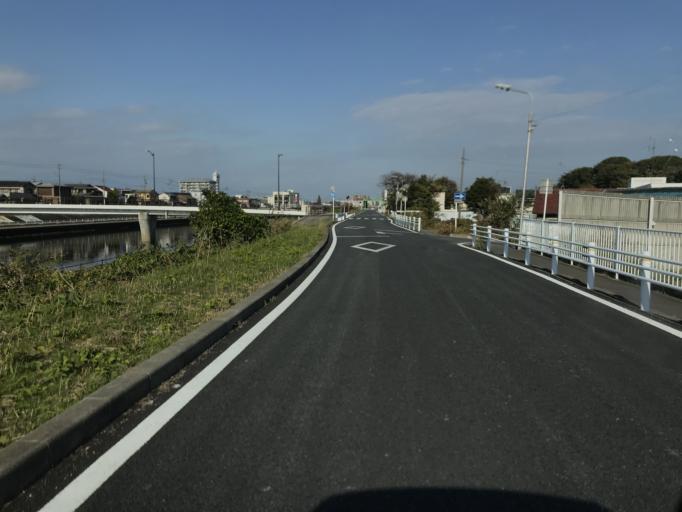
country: JP
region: Aichi
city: Nagoya-shi
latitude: 35.1909
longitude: 136.8492
